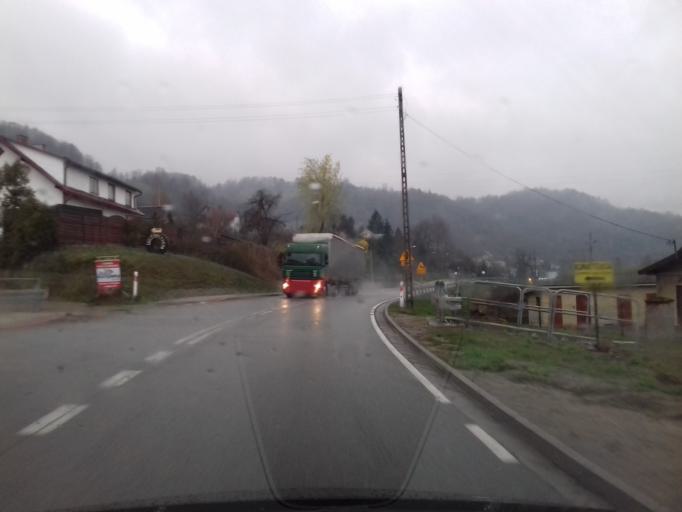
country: PL
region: Lesser Poland Voivodeship
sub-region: Powiat nowosadecki
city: Piwniczna-Zdroj
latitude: 49.4508
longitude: 20.6991
